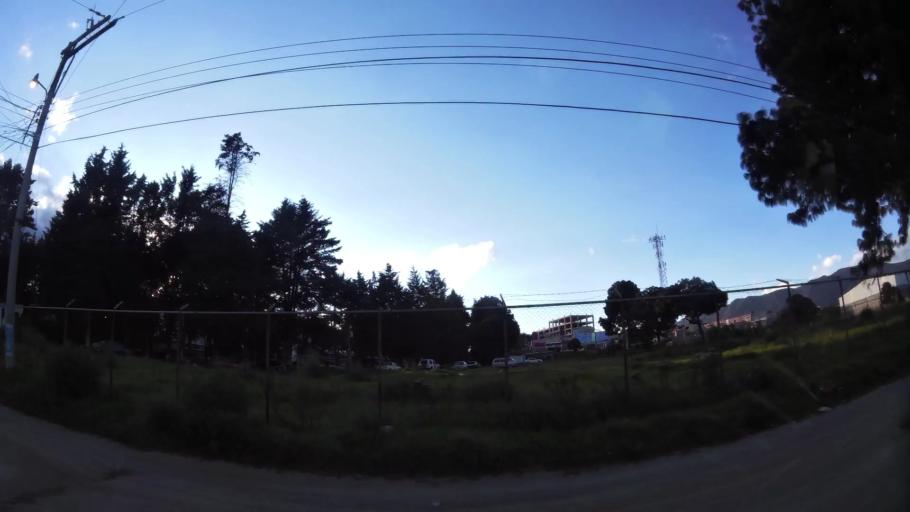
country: GT
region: Quetzaltenango
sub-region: Municipio de La Esperanza
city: La Esperanza
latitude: 14.8607
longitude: -91.5381
